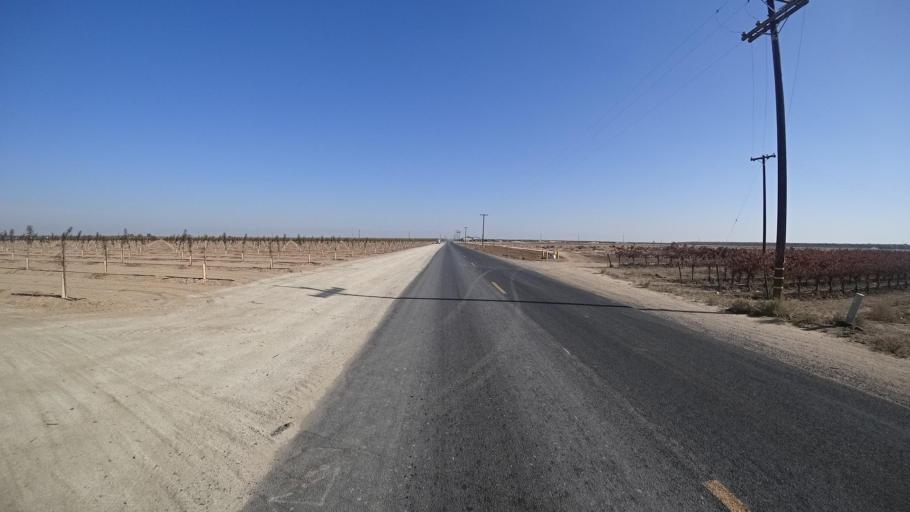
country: US
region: California
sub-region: Kern County
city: McFarland
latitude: 35.6456
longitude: -119.2088
